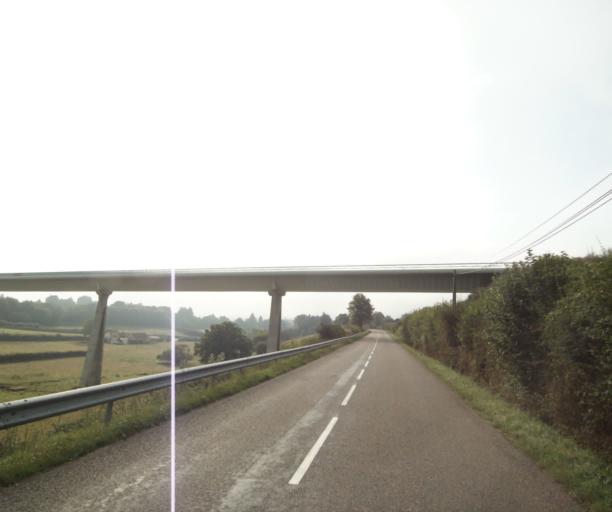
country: FR
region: Bourgogne
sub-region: Departement de Saone-et-Loire
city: Charolles
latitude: 46.4436
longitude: 4.2686
